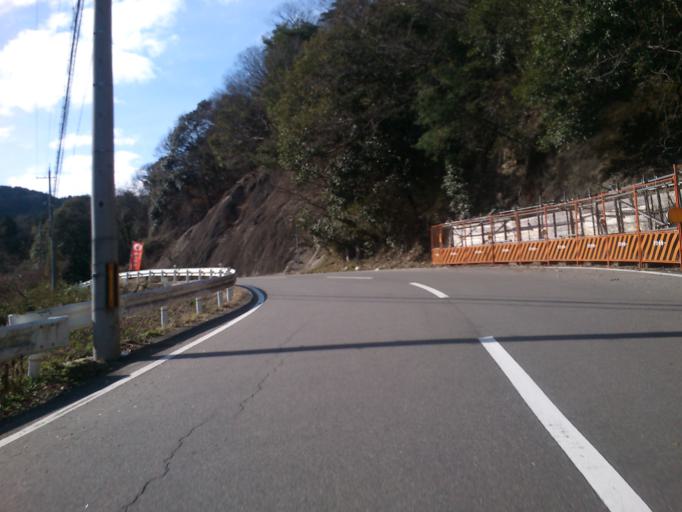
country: JP
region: Kyoto
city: Yawata
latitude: 34.9148
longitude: 135.6567
